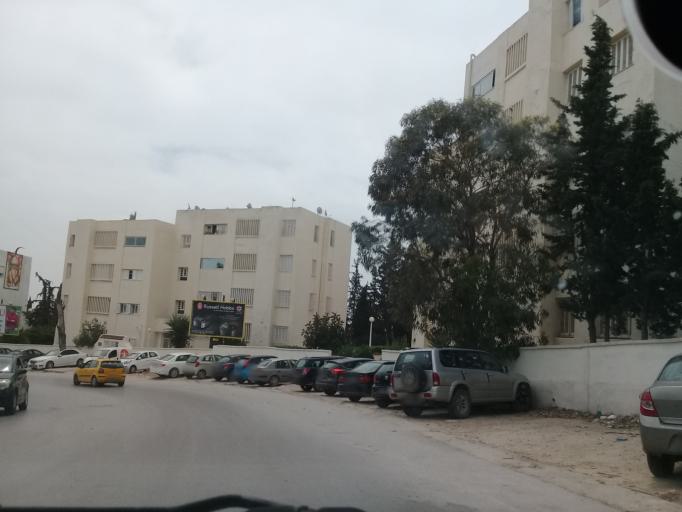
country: TN
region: Tunis
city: Tunis
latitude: 36.8375
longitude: 10.1548
